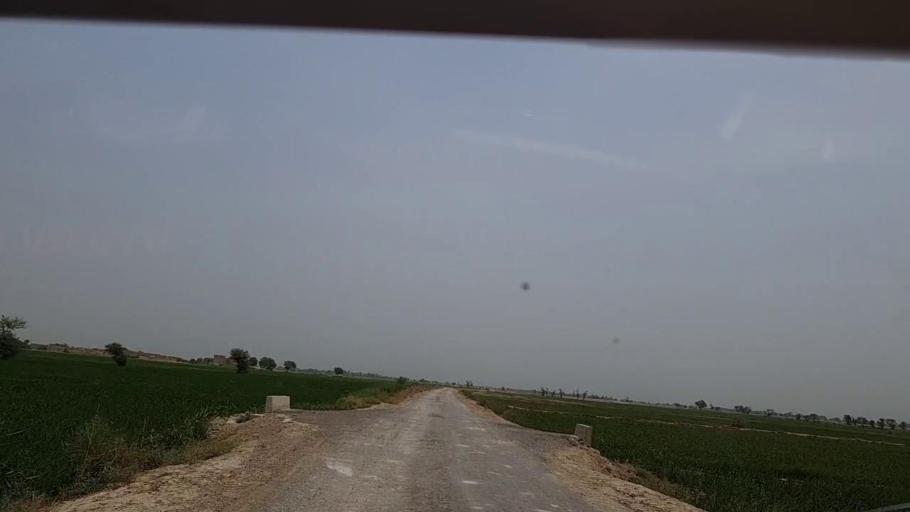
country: PK
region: Sindh
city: Khairpur Nathan Shah
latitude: 27.0161
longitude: 67.6508
